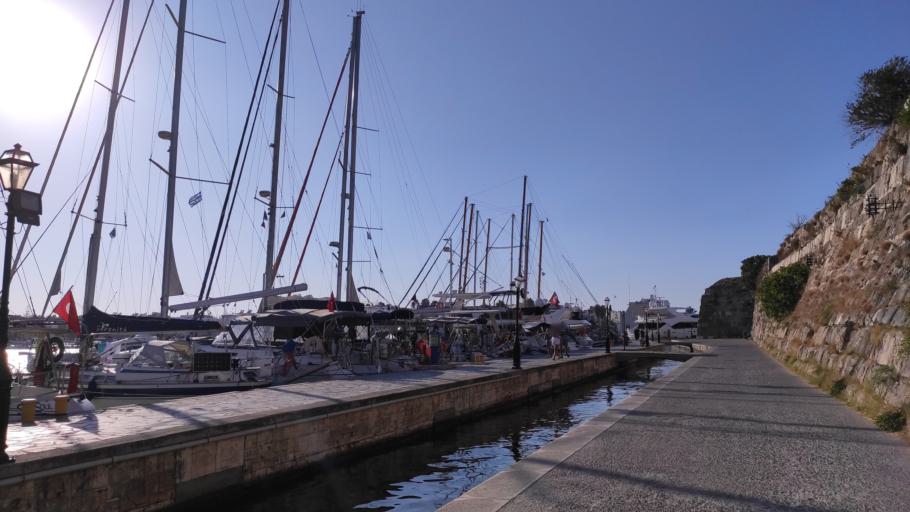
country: GR
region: South Aegean
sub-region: Nomos Dodekanisou
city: Kos
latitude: 36.8956
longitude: 27.2897
